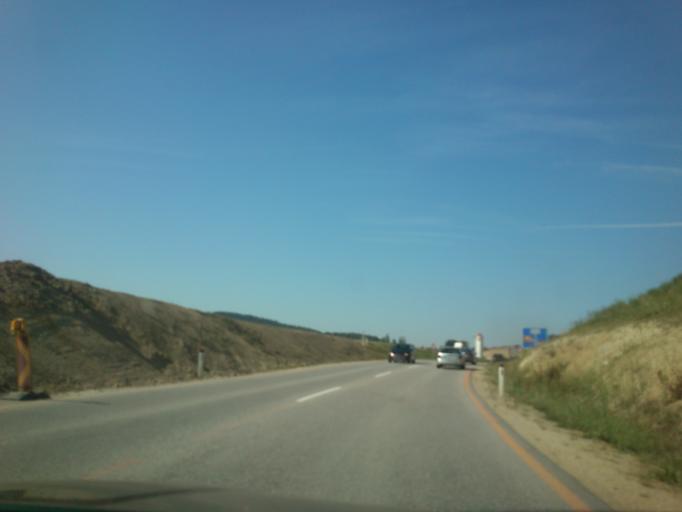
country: AT
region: Upper Austria
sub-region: Politischer Bezirk Freistadt
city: Freistadt
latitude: 48.4498
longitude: 14.4946
